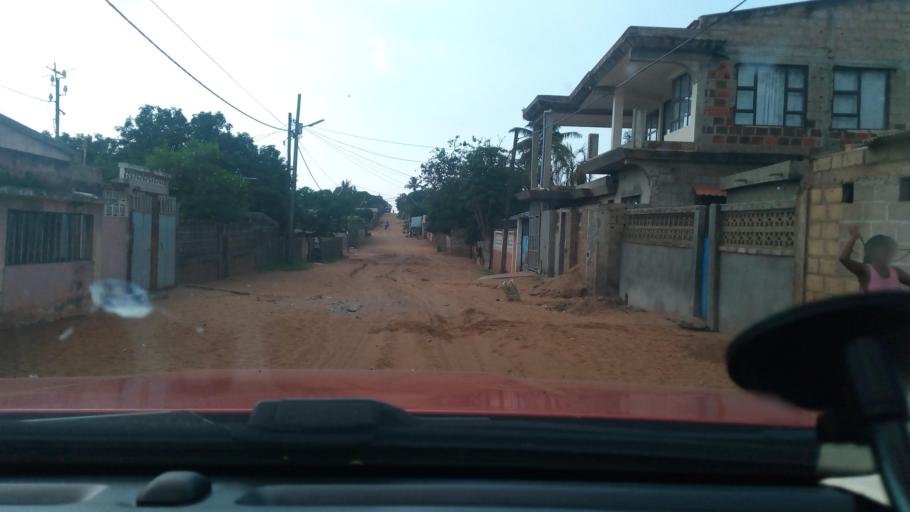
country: MZ
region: Maputo City
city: Maputo
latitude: -25.9209
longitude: 32.5966
